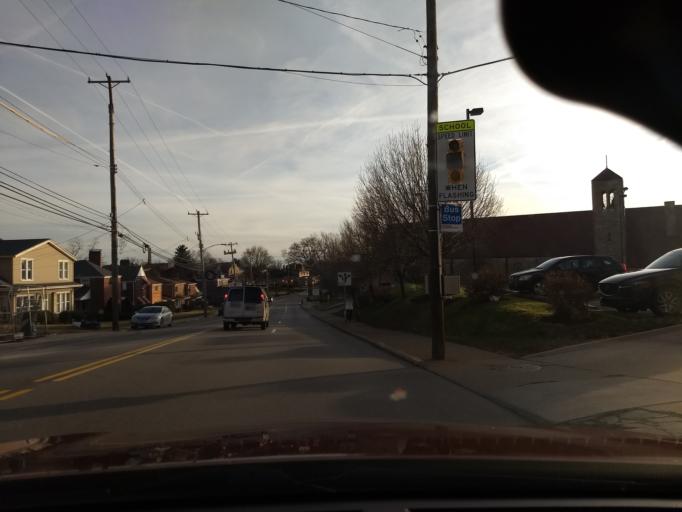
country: US
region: Pennsylvania
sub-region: Allegheny County
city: Brentwood
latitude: 40.3717
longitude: -79.9753
